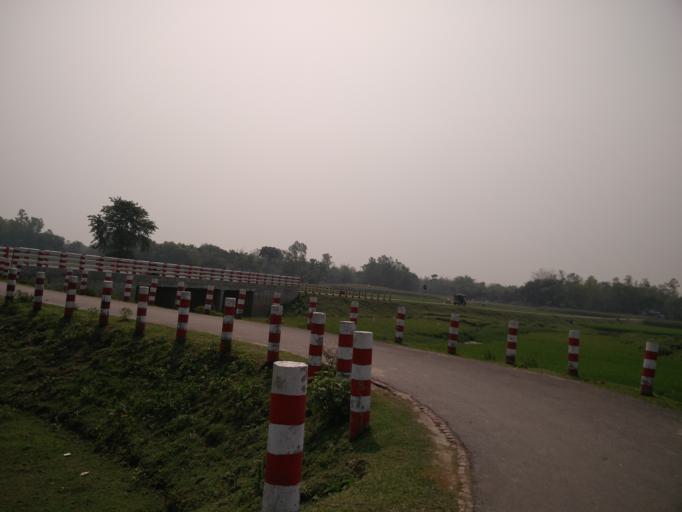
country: BD
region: Dhaka
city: Muktagacha
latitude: 24.9026
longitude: 90.2582
